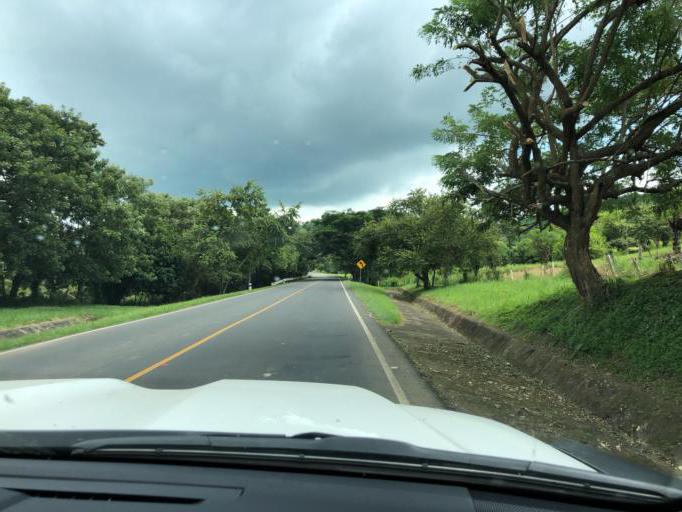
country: NI
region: Chontales
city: Villa Sandino
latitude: 12.0546
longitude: -85.0334
